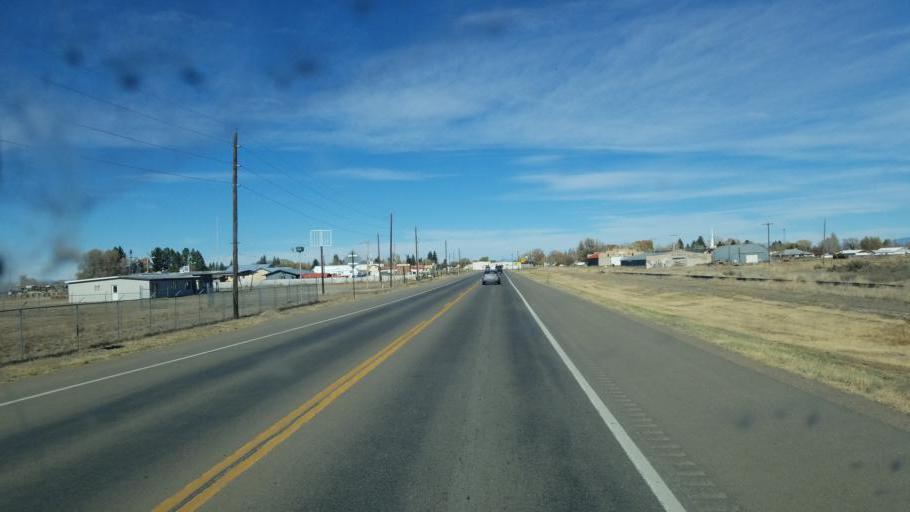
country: US
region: Colorado
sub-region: Conejos County
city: Conejos
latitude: 37.2653
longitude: -105.9637
